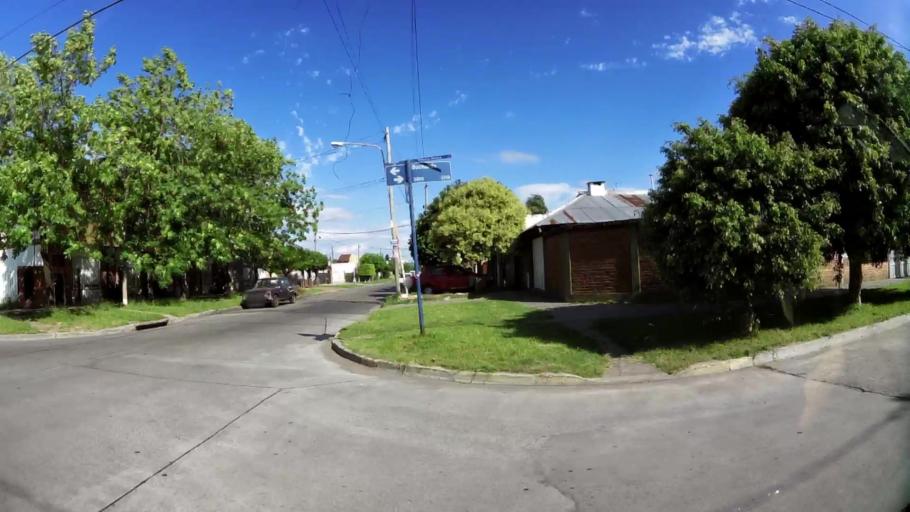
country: AR
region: Buenos Aires
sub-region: Partido de Moron
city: Moron
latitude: -34.6614
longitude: -58.5930
